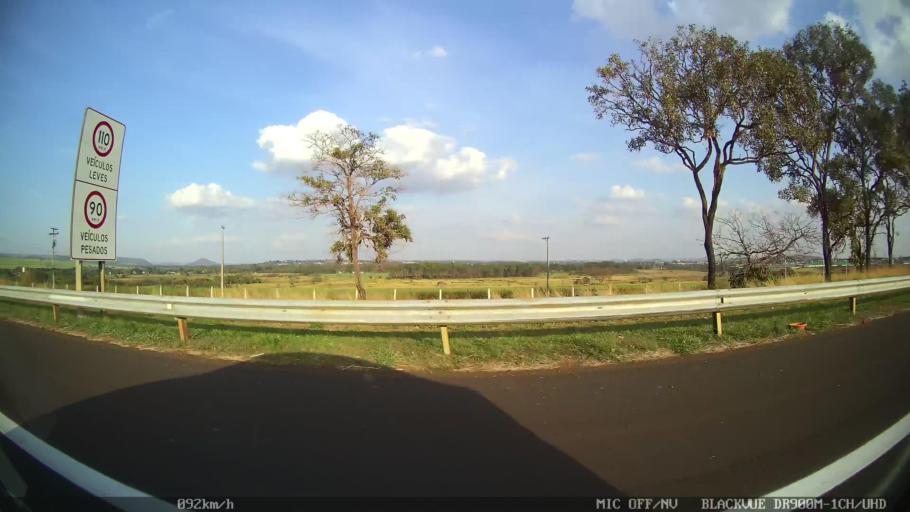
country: BR
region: Sao Paulo
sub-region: Ribeirao Preto
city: Ribeirao Preto
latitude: -21.1078
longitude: -47.7703
